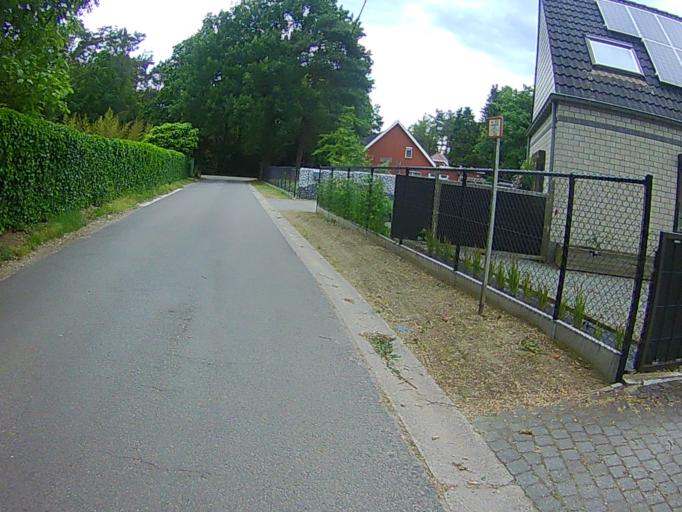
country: BE
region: Flanders
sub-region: Provincie Vlaams-Brabant
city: Keerbergen
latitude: 51.0102
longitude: 4.6178
